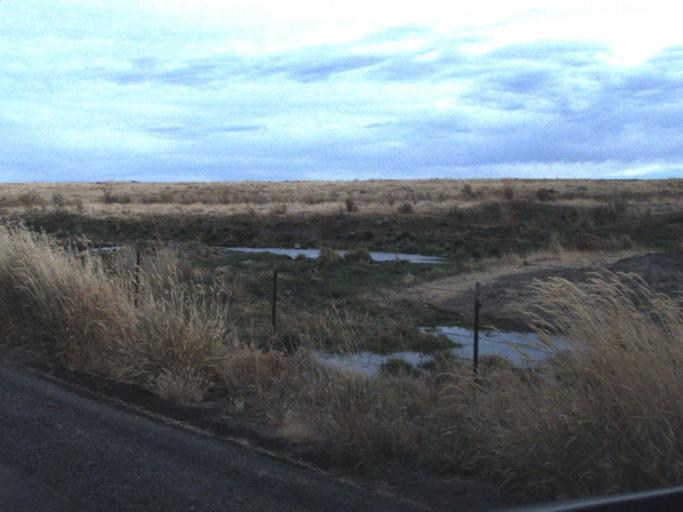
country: US
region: Washington
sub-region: Okanogan County
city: Coulee Dam
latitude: 47.6906
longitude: -118.7219
